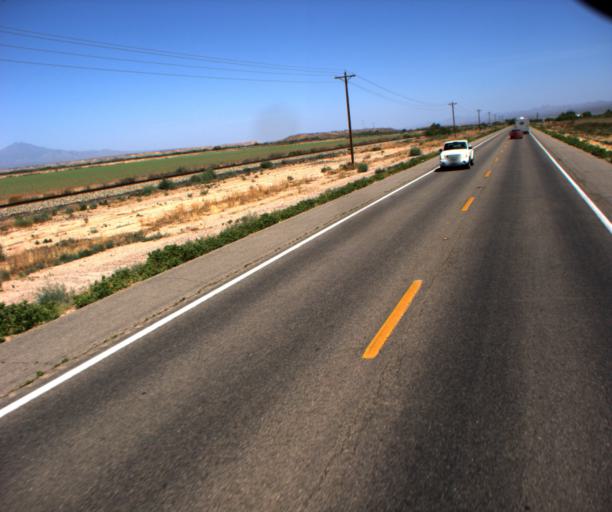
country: US
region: Arizona
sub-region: Graham County
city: Pima
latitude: 32.9774
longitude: -109.9293
